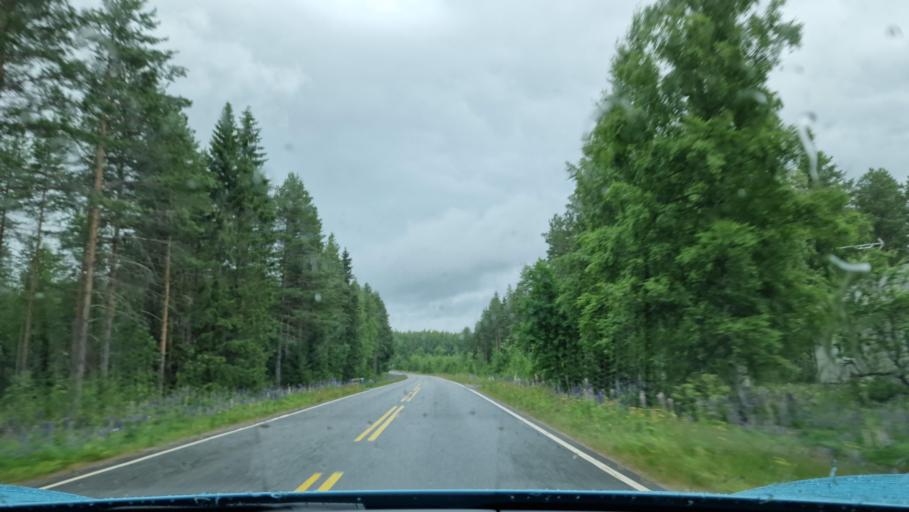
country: FI
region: Southern Ostrobothnia
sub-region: Jaerviseutu
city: Soini
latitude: 62.7996
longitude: 24.3728
